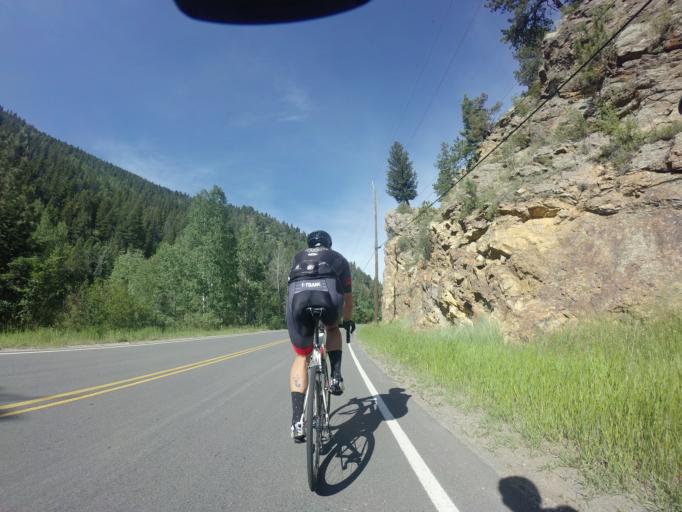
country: US
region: Colorado
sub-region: Clear Creek County
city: Idaho Springs
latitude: 39.7250
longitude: -105.5559
